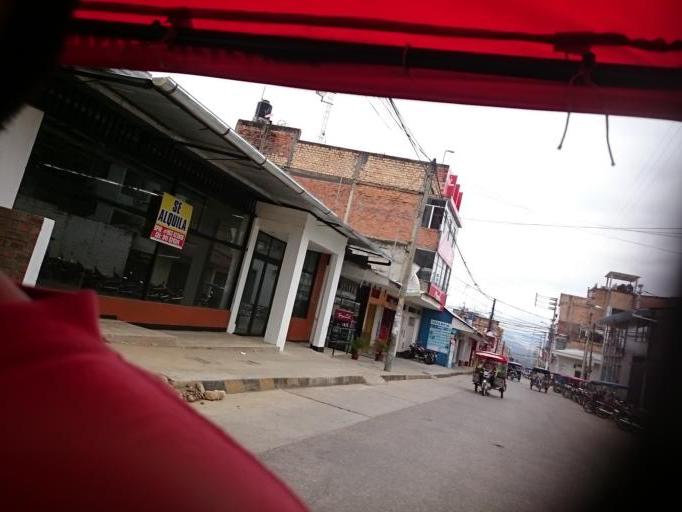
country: PE
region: San Martin
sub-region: Provincia de San Martin
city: Tarapoto
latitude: -6.4872
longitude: -76.3614
